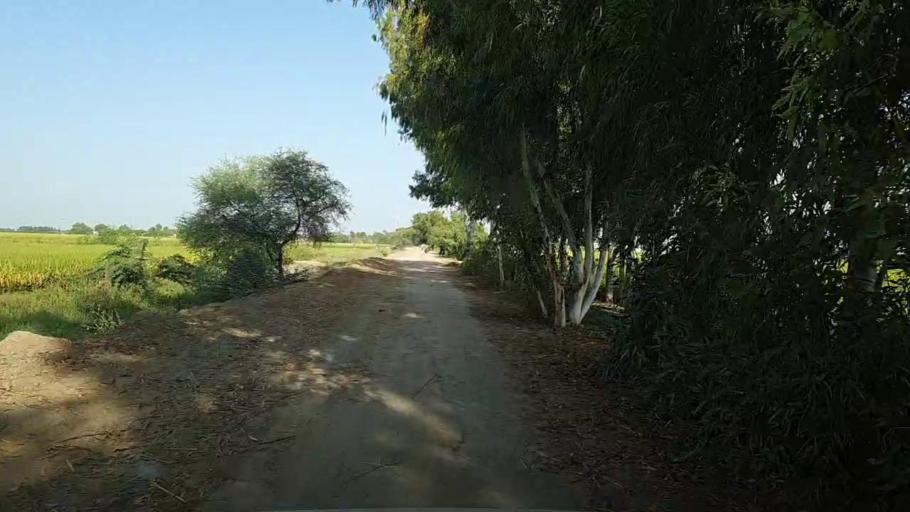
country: PK
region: Sindh
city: Kario
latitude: 24.5996
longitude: 68.5196
